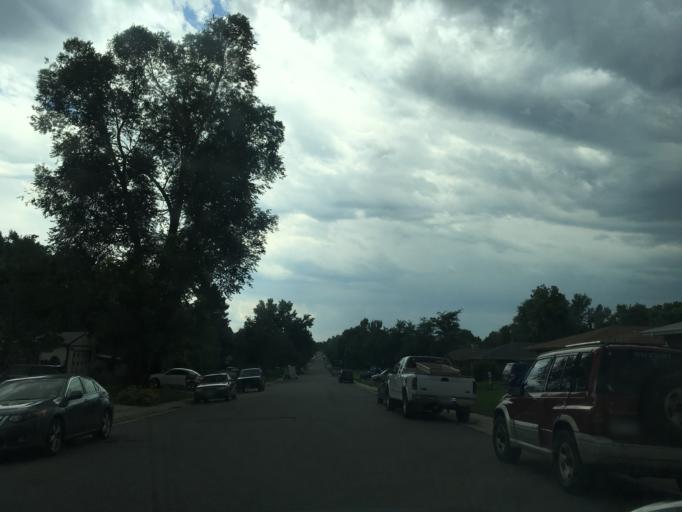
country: US
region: Colorado
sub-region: Arapahoe County
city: Sheridan
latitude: 39.6741
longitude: -105.0378
